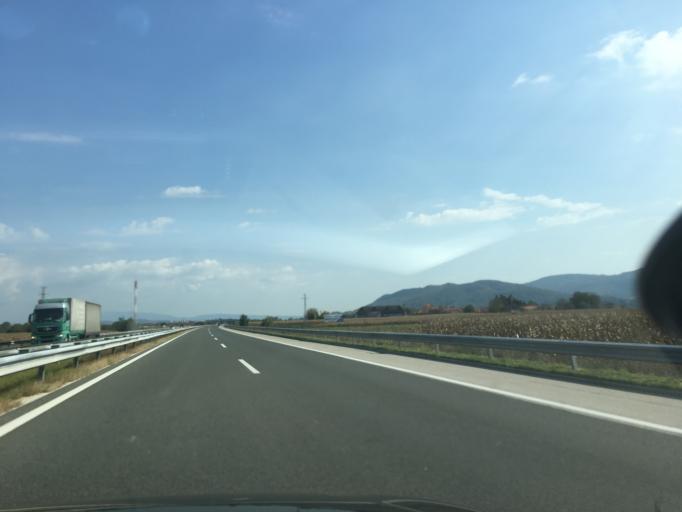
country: SI
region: Brezice
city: Brezice
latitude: 45.9095
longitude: 15.5393
